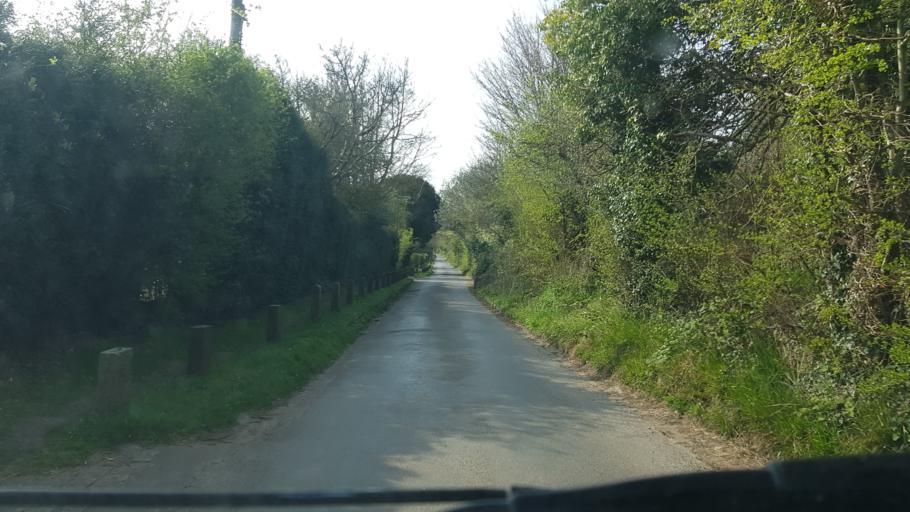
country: GB
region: England
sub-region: Surrey
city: Chilworth
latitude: 51.2316
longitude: -0.5307
